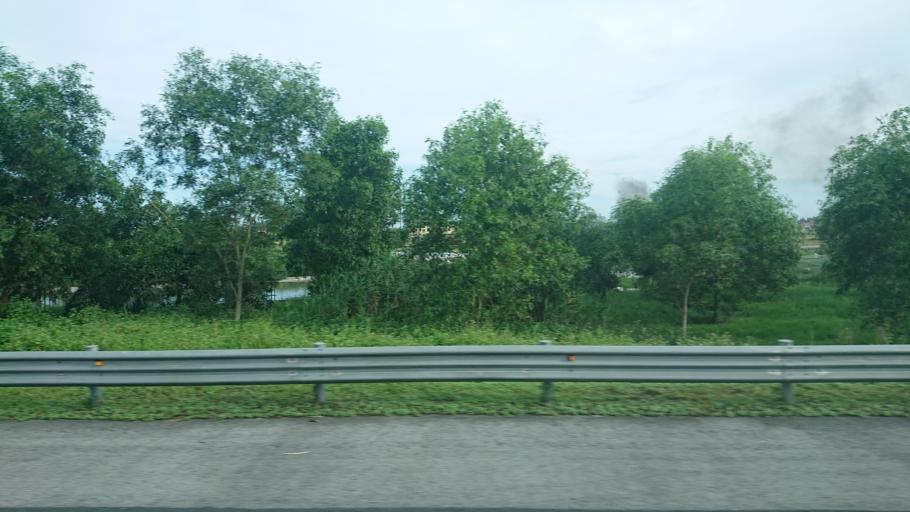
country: VN
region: Hai Phong
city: Nui Doi
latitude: 20.7656
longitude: 106.6554
